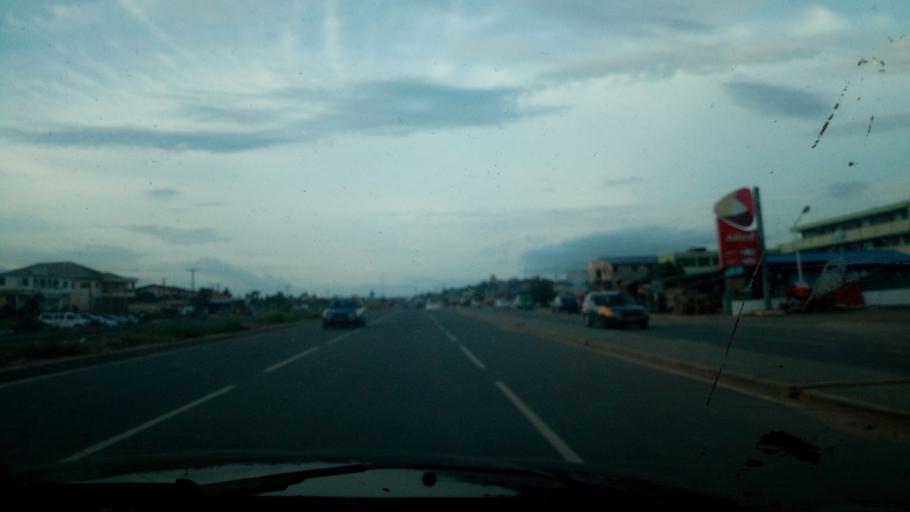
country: GH
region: Western
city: Takoradi
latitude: 4.9252
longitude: -1.7831
